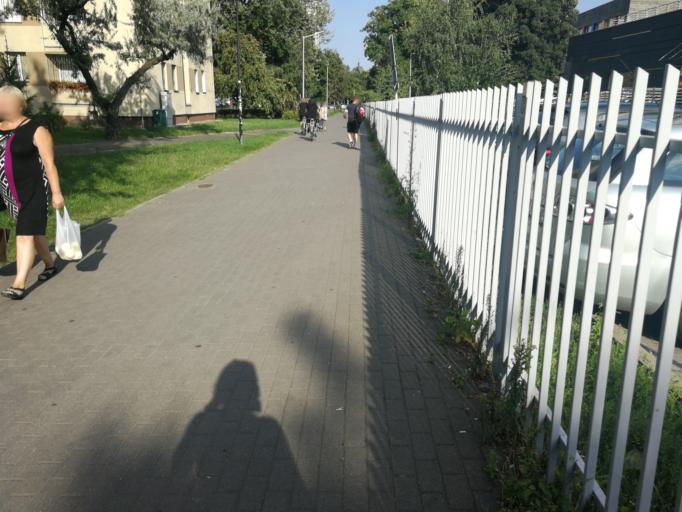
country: PL
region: Masovian Voivodeship
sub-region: Warszawa
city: Targowek
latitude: 52.2866
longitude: 21.0374
